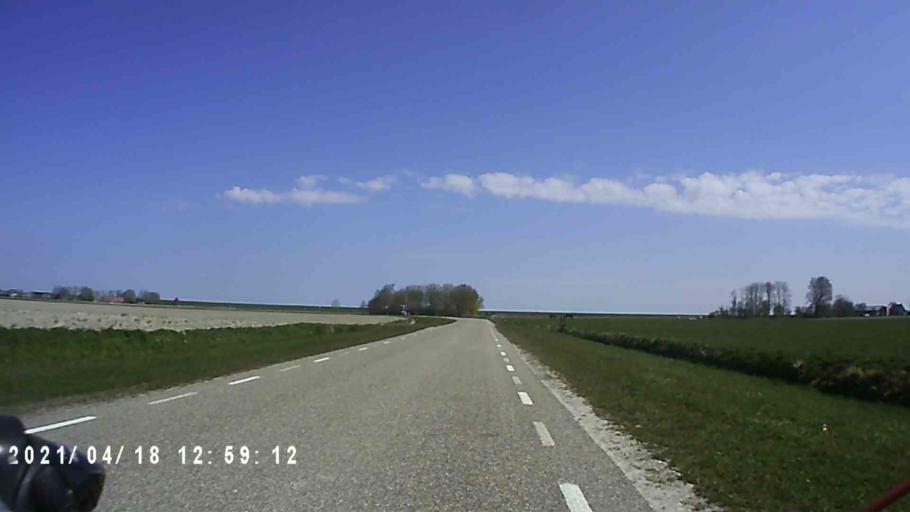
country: NL
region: Friesland
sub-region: Gemeente Dongeradeel
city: Anjum
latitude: 53.3952
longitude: 6.0887
